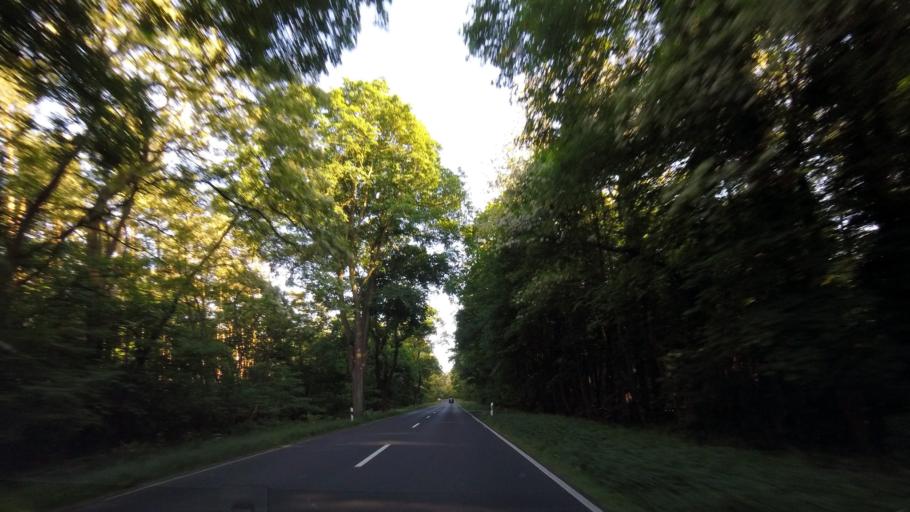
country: DE
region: Brandenburg
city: Golzow
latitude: 52.3300
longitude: 12.6040
